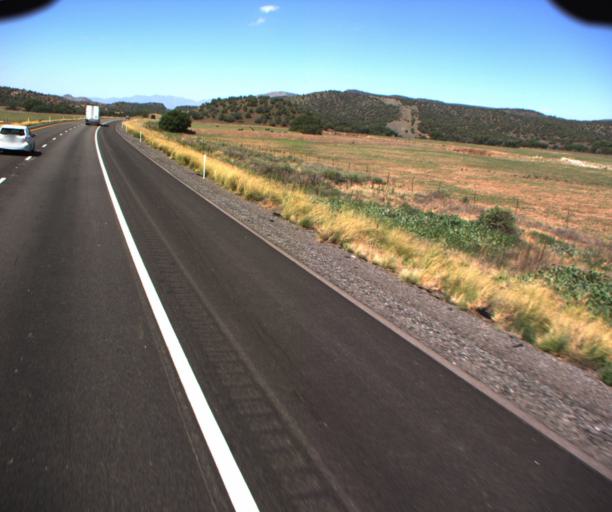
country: US
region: Arizona
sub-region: Mohave County
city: Peach Springs
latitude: 35.1864
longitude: -113.4509
